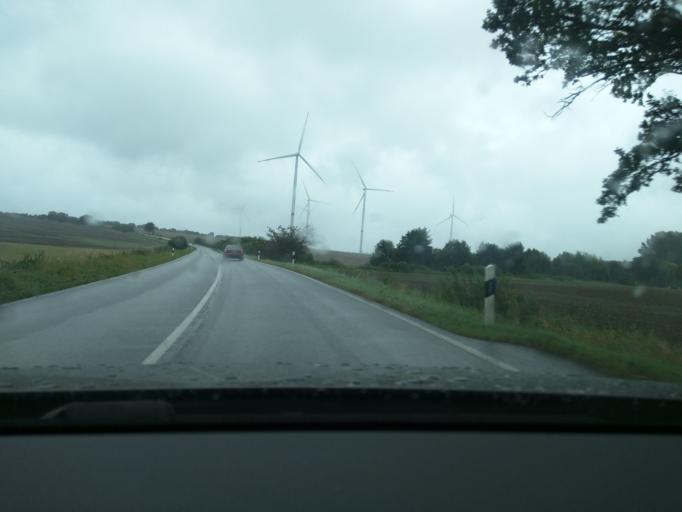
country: DE
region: Schleswig-Holstein
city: Wangelau
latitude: 53.4417
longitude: 10.5584
